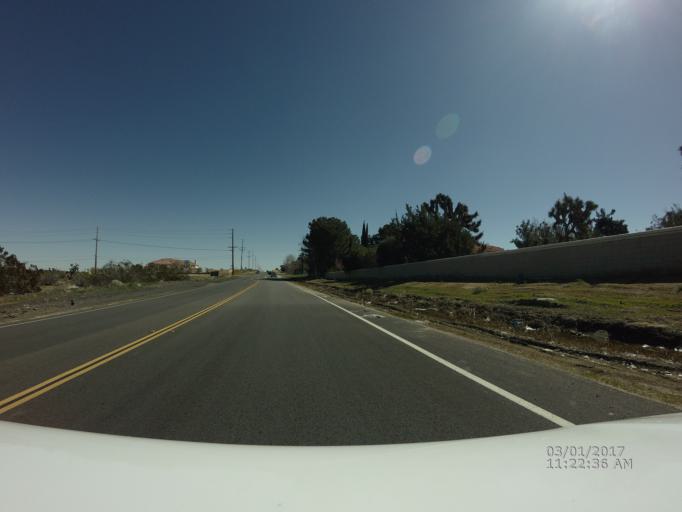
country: US
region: California
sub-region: Los Angeles County
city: Quartz Hill
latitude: 34.6456
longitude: -118.1936
